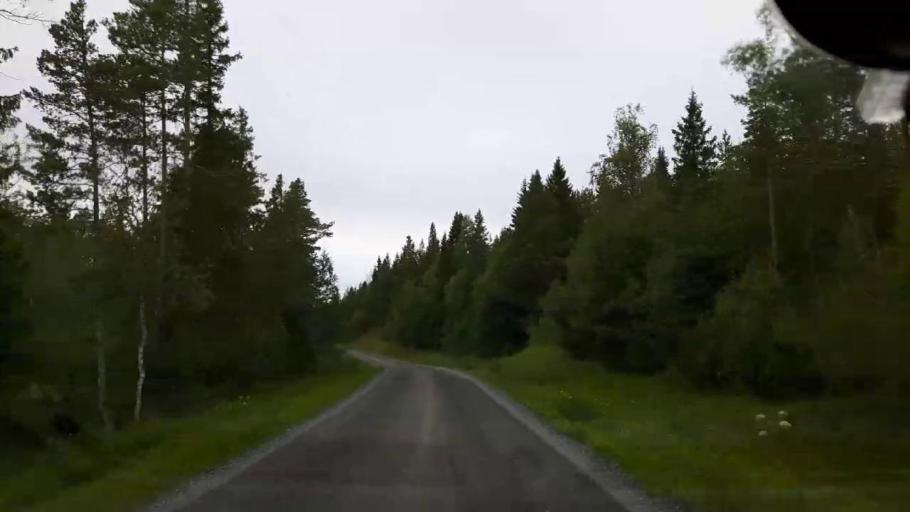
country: SE
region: Jaemtland
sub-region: Krokoms Kommun
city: Krokom
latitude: 63.2970
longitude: 14.3647
